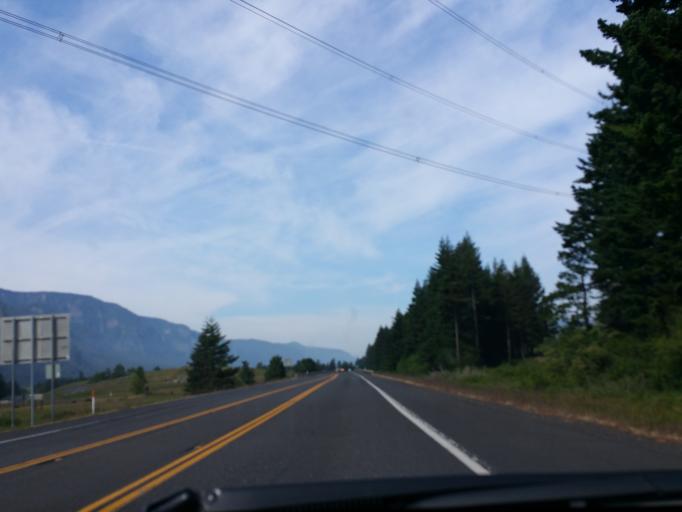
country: US
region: Oregon
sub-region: Hood River County
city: Cascade Locks
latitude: 45.6457
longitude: -121.9584
